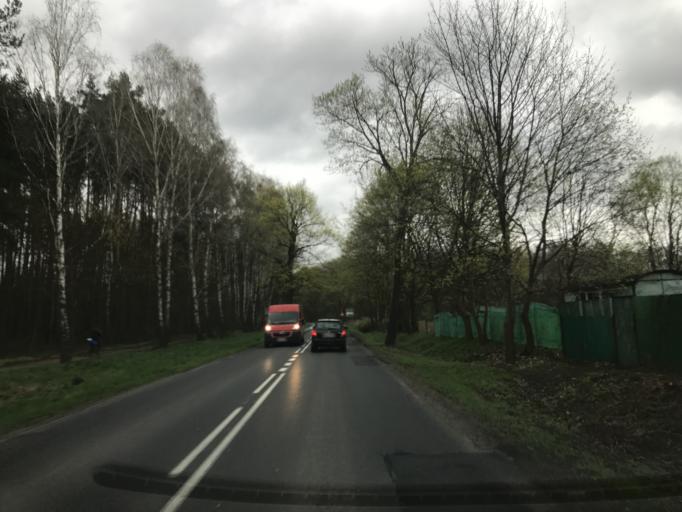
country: PL
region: Kujawsko-Pomorskie
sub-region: Bydgoszcz
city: Fordon
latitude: 53.1380
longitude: 18.1905
